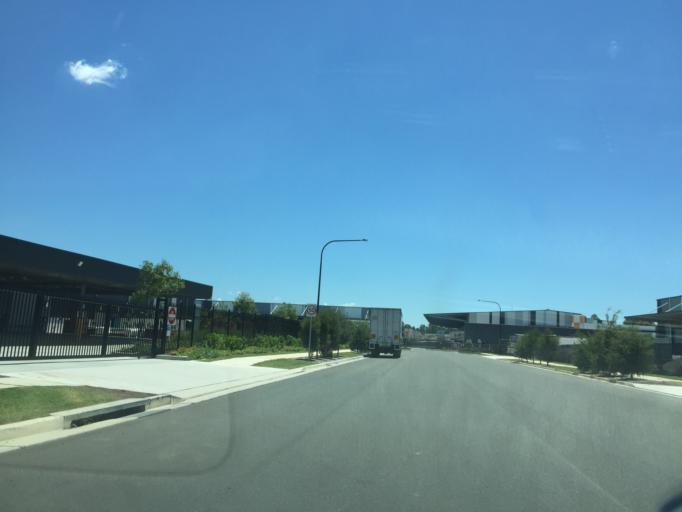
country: AU
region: New South Wales
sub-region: Blacktown
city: Doonside
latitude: -33.7953
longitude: 150.8684
